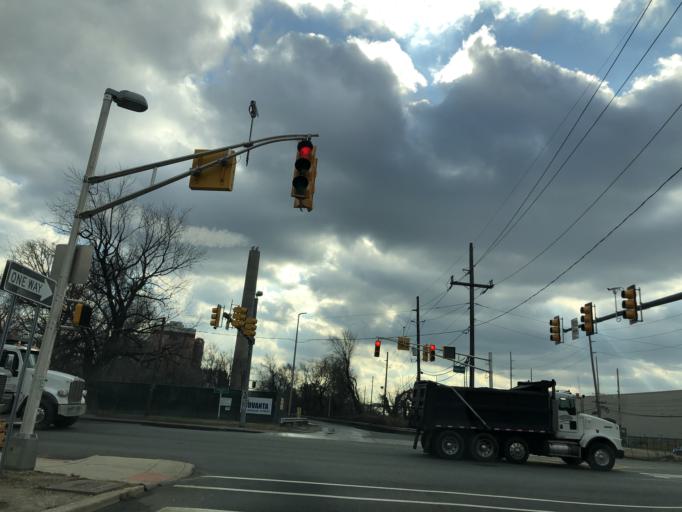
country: US
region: New Jersey
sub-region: Camden County
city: Camden
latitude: 39.9129
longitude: -75.1174
